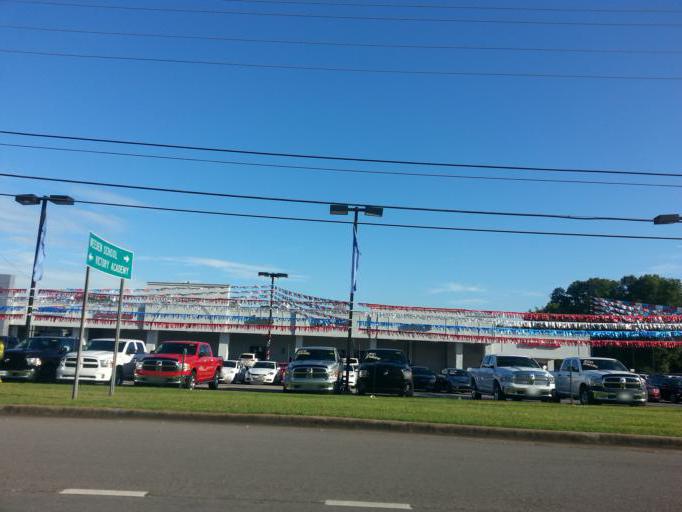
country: US
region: Alabama
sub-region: Lauderdale County
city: East Florence
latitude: 34.8270
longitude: -87.6403
